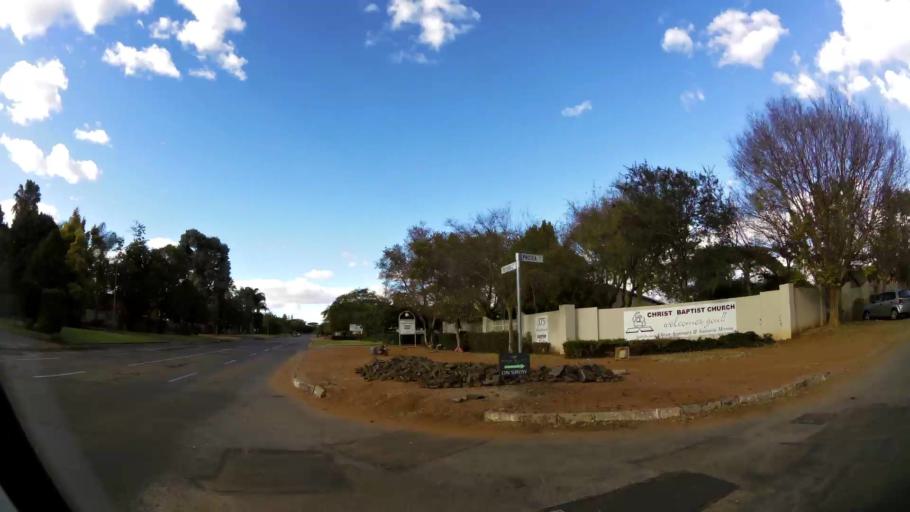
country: ZA
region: Limpopo
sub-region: Capricorn District Municipality
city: Polokwane
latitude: -23.9063
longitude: 29.4945
